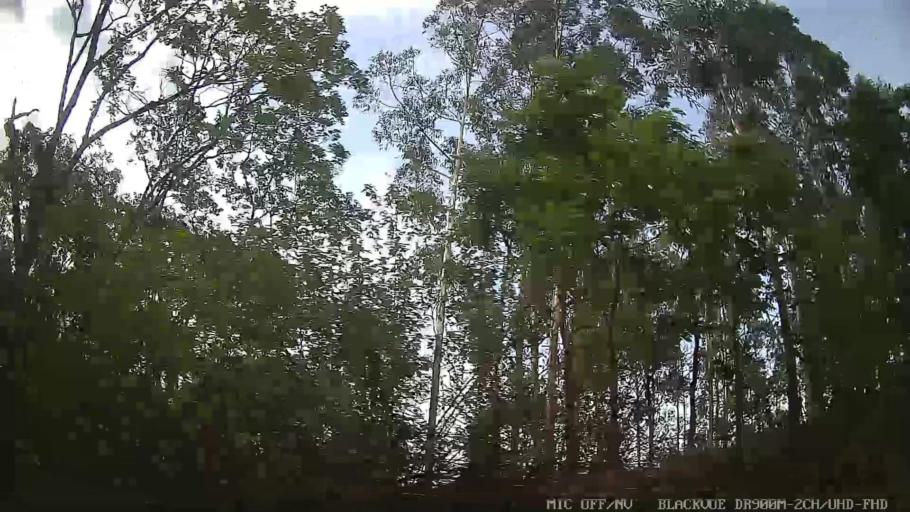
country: BR
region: Sao Paulo
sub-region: Amparo
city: Amparo
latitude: -22.7817
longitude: -46.7607
